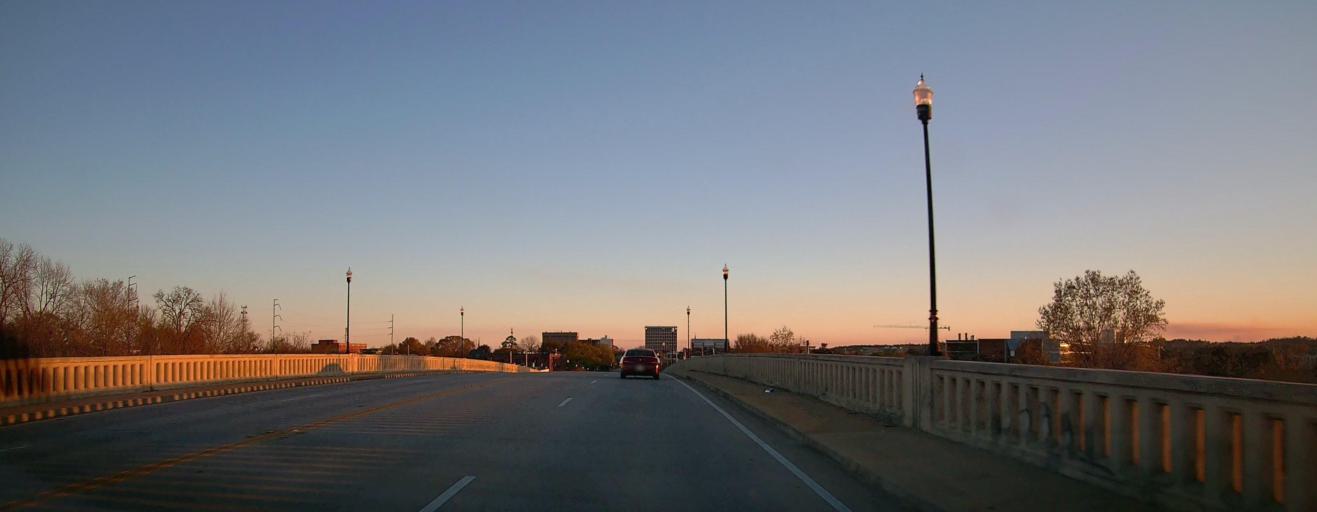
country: US
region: Alabama
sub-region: Russell County
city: Phenix City
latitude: 32.4775
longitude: -84.9905
